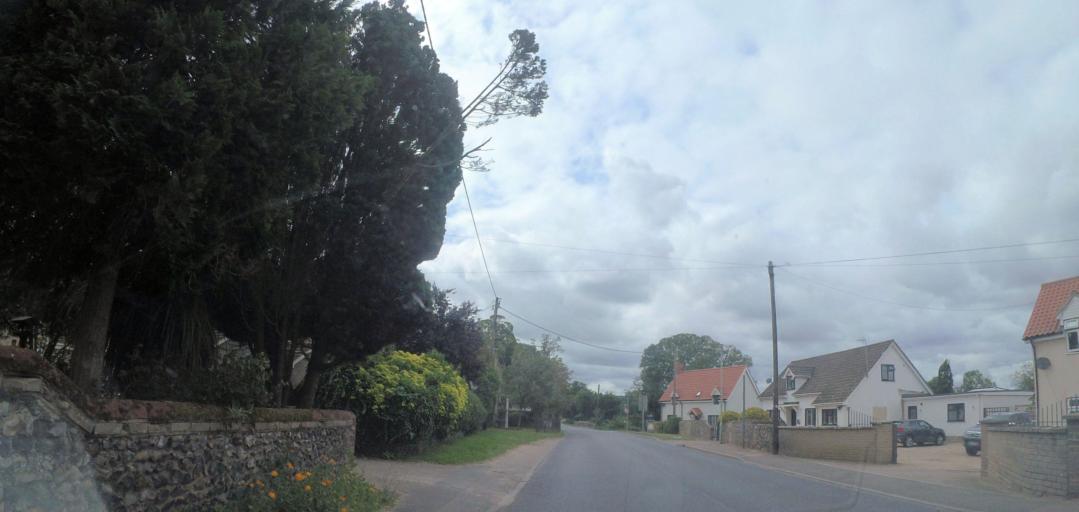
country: GB
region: England
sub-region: Suffolk
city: Lakenheath
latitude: 52.3166
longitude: 0.5428
